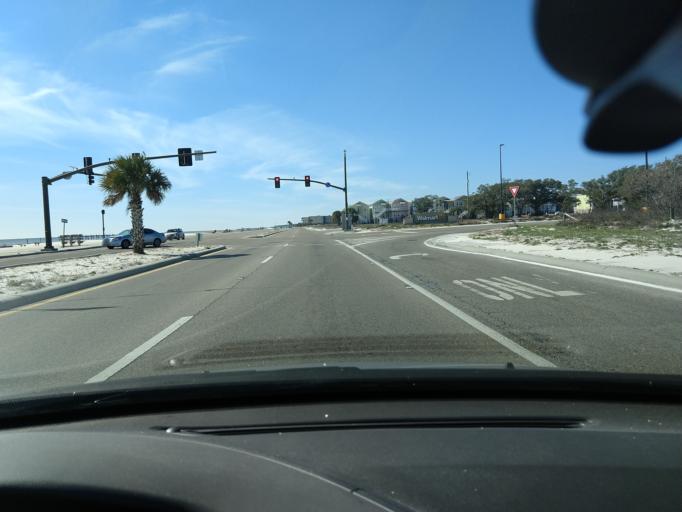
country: US
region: Mississippi
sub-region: Harrison County
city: Long Beach
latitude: 30.3316
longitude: -89.1893
